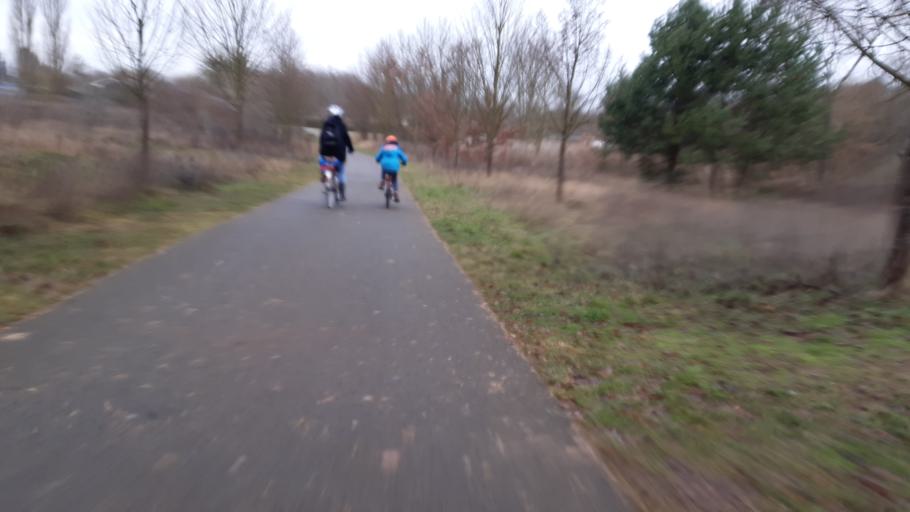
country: DE
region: Brandenburg
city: Templin
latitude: 53.1161
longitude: 13.5184
